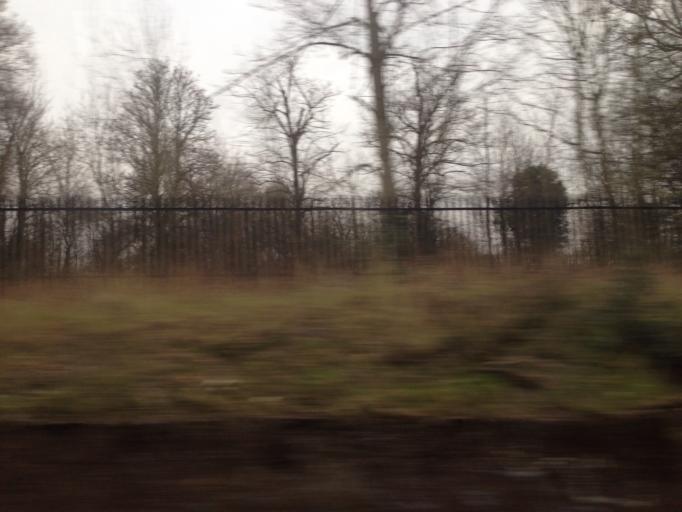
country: GB
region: England
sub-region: Greater London
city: Brixton Hill
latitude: 51.4363
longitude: -0.1405
